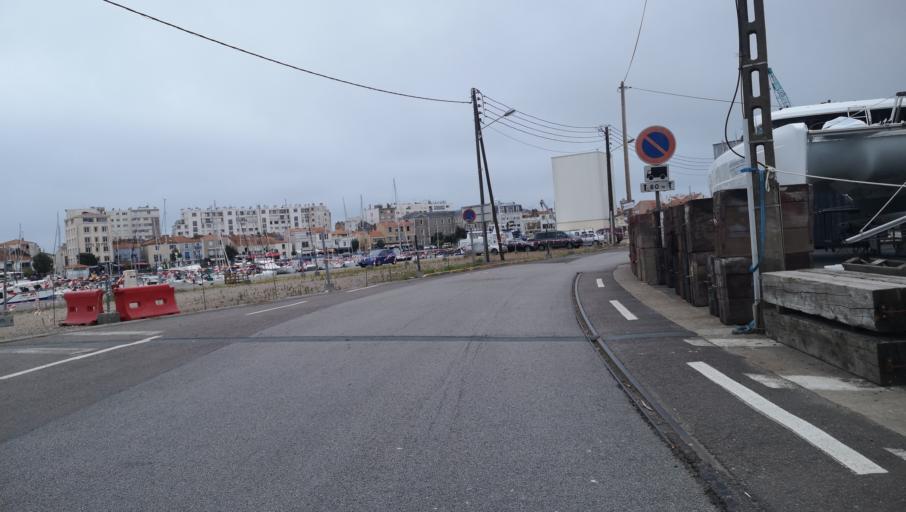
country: FR
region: Pays de la Loire
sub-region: Departement de la Vendee
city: Les Sables-d'Olonne
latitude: 46.4981
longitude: -1.7897
